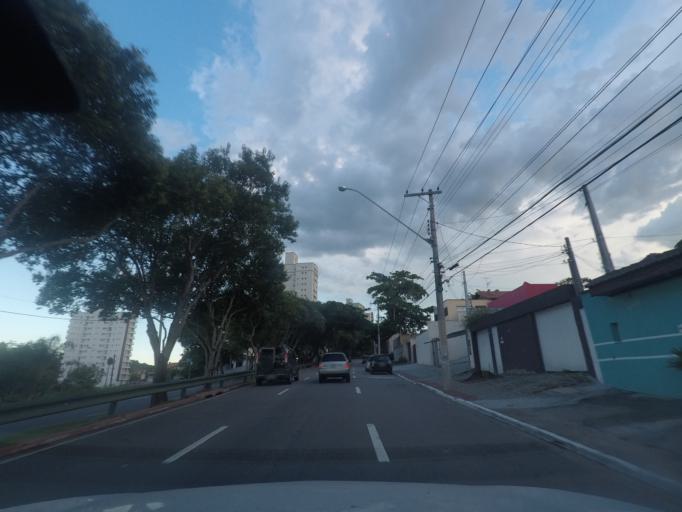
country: BR
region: Sao Paulo
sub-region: Sao Jose Dos Campos
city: Sao Jose dos Campos
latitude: -23.2247
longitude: -45.8812
